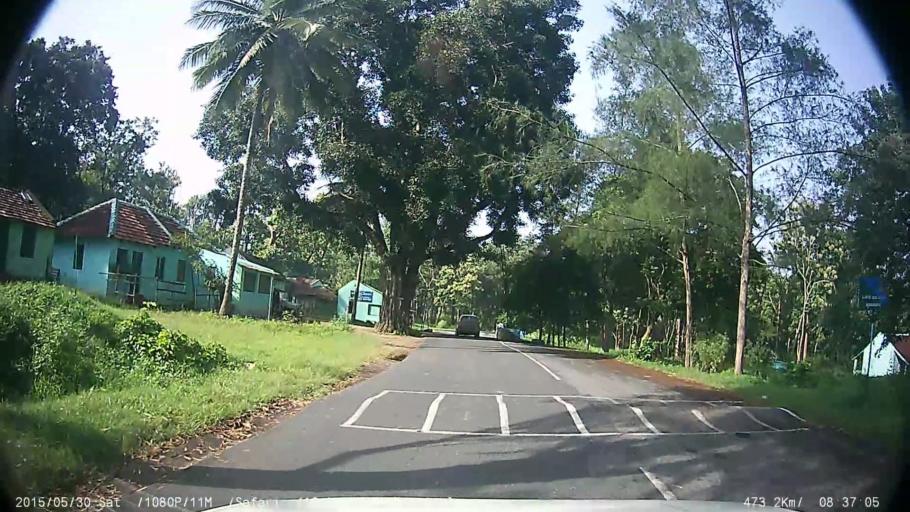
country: IN
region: Karnataka
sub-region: Mysore
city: Sargur
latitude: 11.7220
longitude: 76.4268
